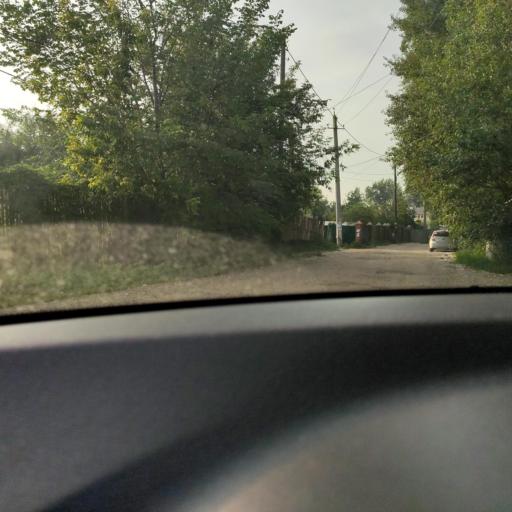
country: RU
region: Samara
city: Rozhdestveno
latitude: 53.1494
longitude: 50.0245
